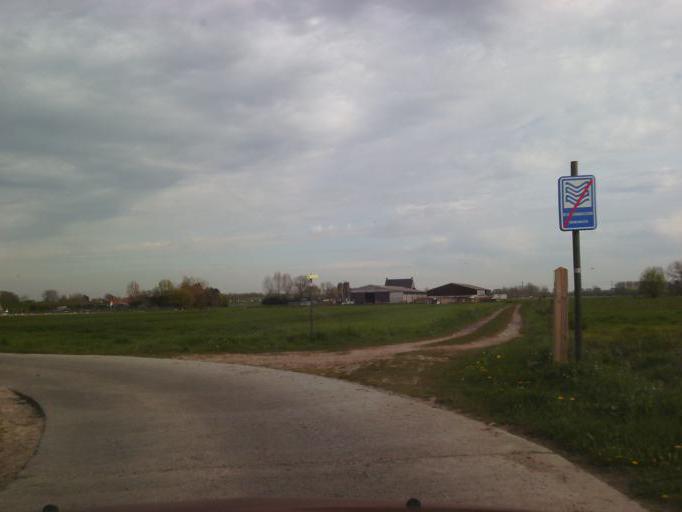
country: BE
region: Flanders
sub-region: Provincie Oost-Vlaanderen
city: Berlare
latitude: 51.0344
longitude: 4.0262
